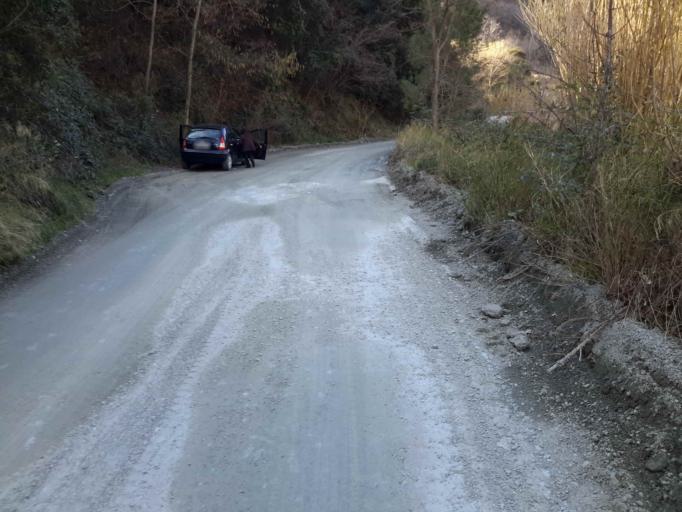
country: IT
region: Liguria
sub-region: Provincia di Savona
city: Albisola Superiore
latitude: 44.3521
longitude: 8.4824
